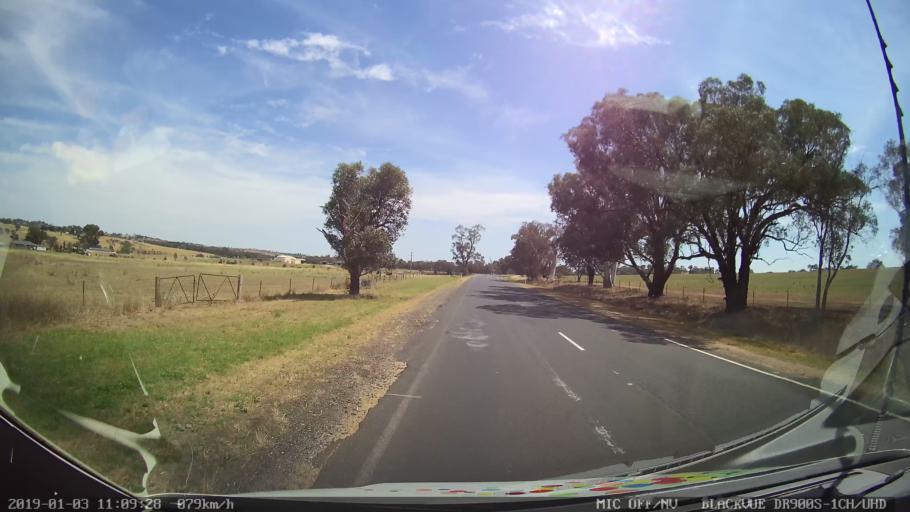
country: AU
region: New South Wales
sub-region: Young
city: Young
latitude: -34.2379
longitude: 148.2554
